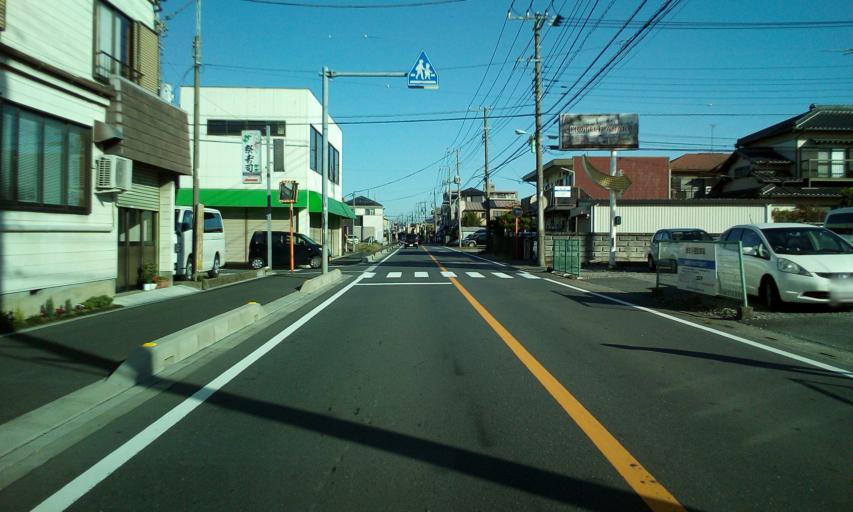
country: JP
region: Chiba
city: Matsudo
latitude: 35.7902
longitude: 139.8848
